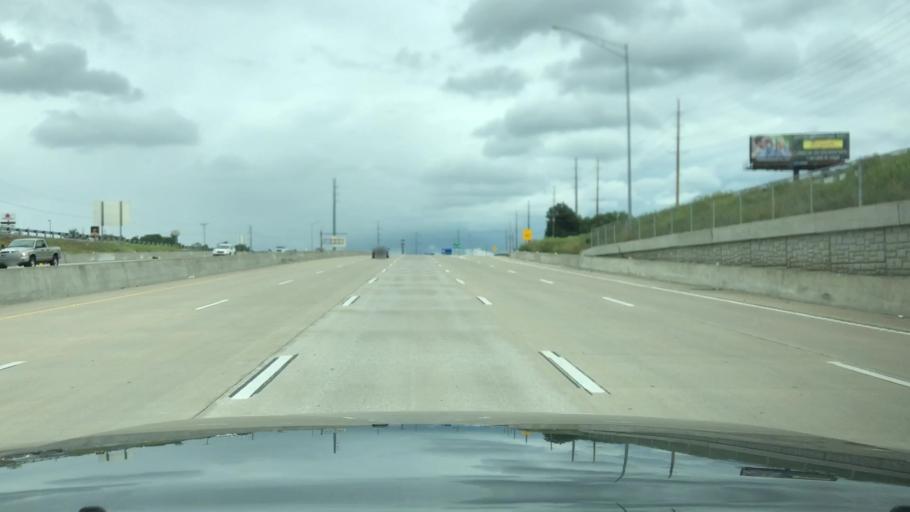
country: US
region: Missouri
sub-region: Saint Charles County
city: Cottleville
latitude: 38.7430
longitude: -90.6061
